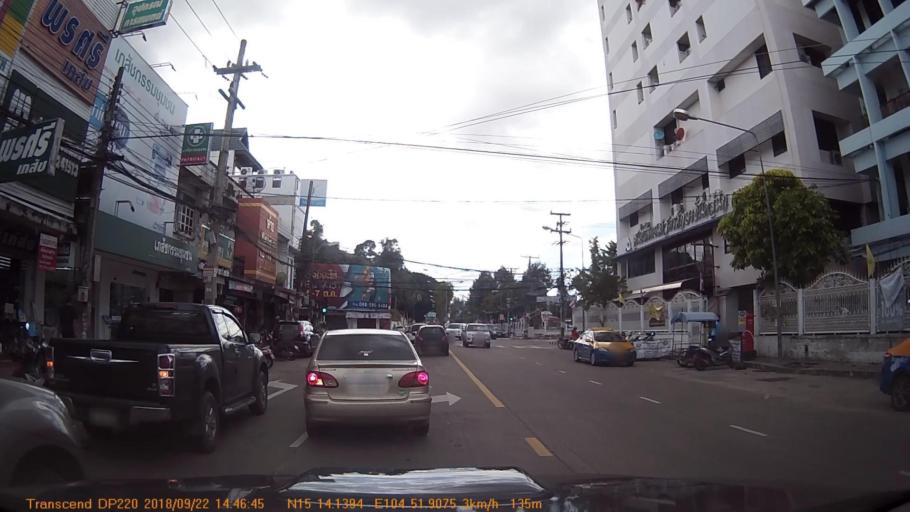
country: TH
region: Changwat Ubon Ratchathani
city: Ubon Ratchathani
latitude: 15.2357
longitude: 104.8649
